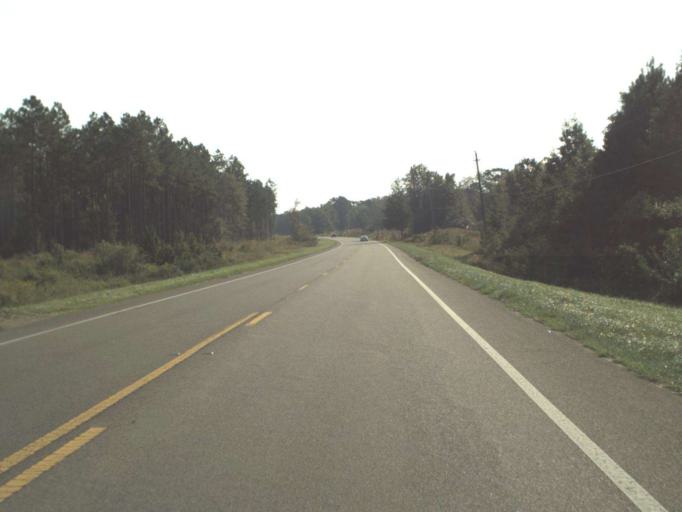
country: US
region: Florida
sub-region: Holmes County
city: Bonifay
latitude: 30.6049
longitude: -85.7375
